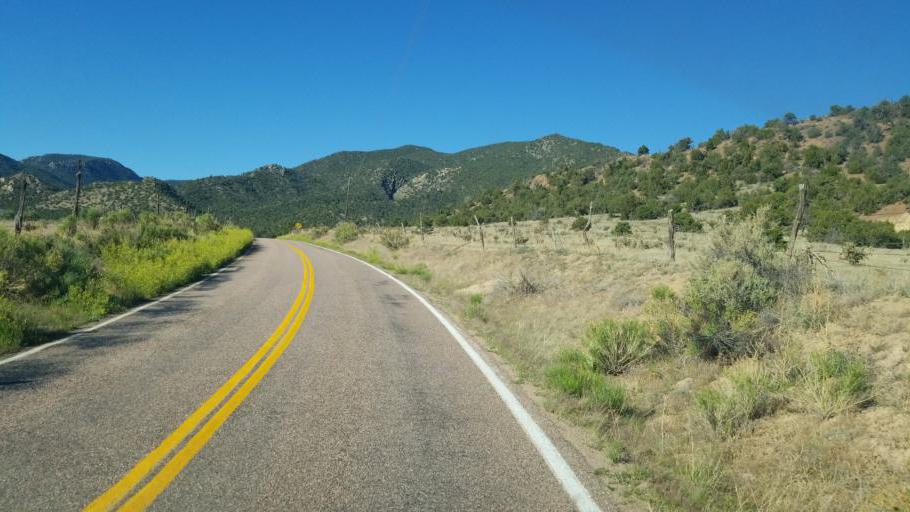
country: US
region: Colorado
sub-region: Fremont County
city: Canon City
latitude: 38.4380
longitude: -105.3798
